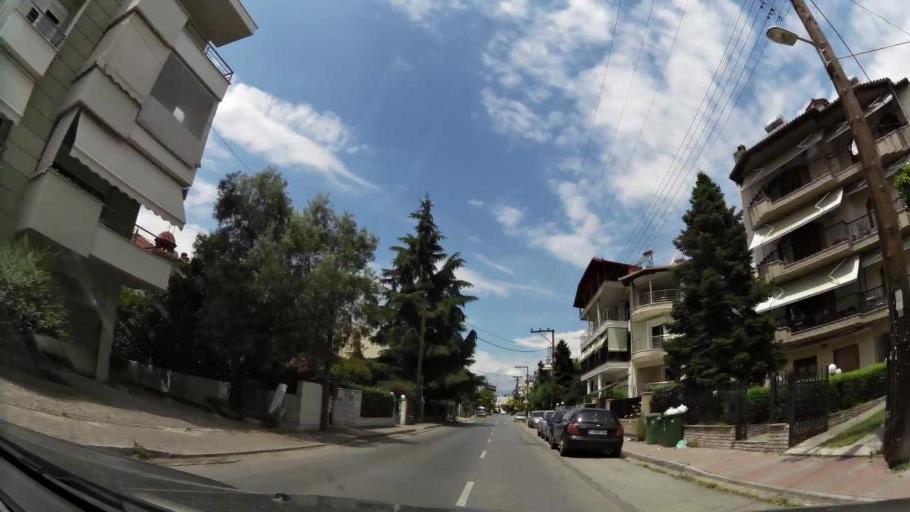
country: GR
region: Central Macedonia
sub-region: Nomos Pierias
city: Katerini
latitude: 40.2665
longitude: 22.5189
